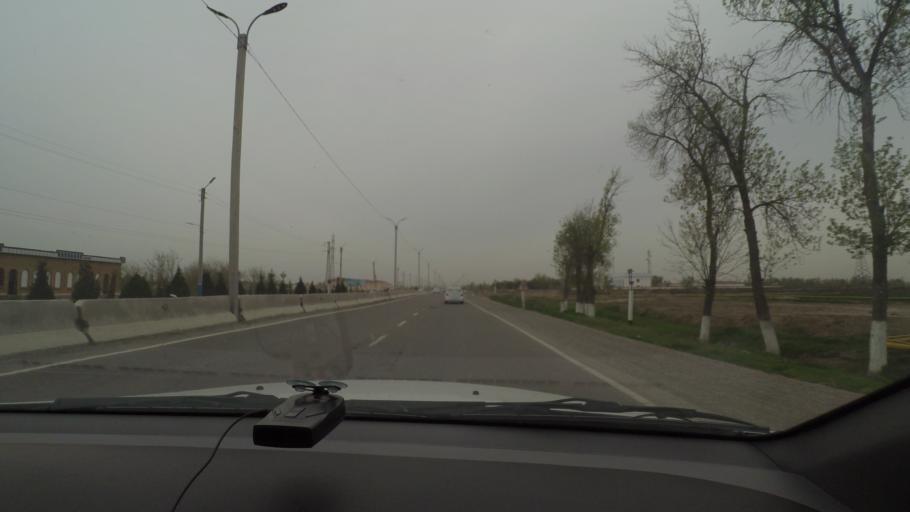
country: KZ
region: Ongtustik Qazaqstan
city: Myrzakent
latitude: 40.5504
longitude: 68.4020
